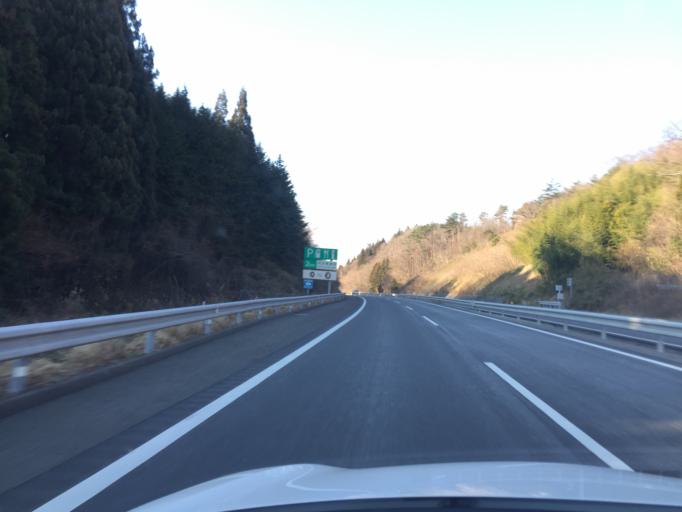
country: JP
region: Fukushima
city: Funehikimachi-funehiki
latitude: 37.3682
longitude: 140.6057
